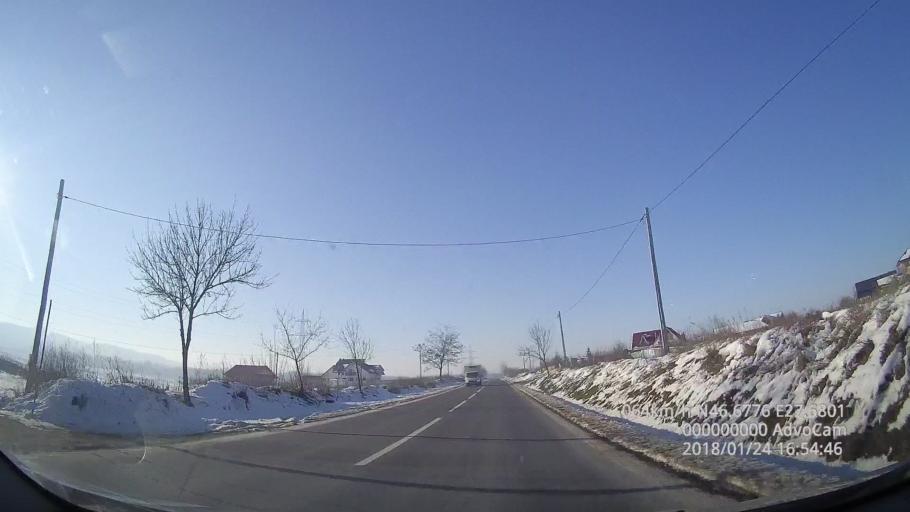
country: RO
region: Vaslui
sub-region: Municipiul Vaslui
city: Brodoc
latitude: 46.6777
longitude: 27.6797
